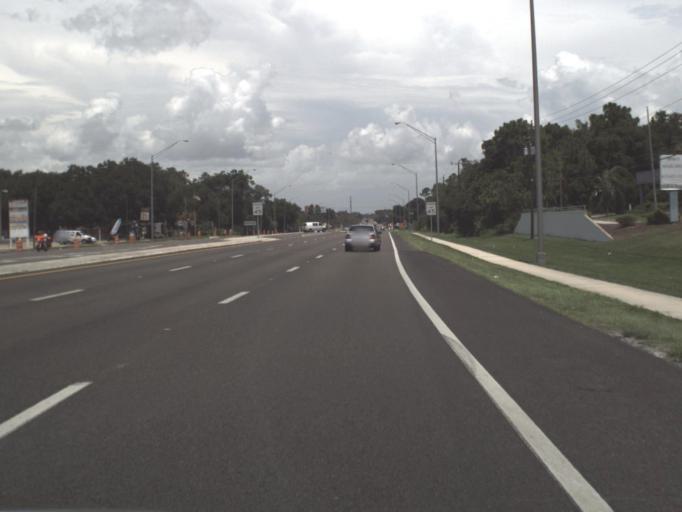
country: US
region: Florida
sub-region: Hillsborough County
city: Riverview
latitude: 27.8587
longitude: -82.3265
